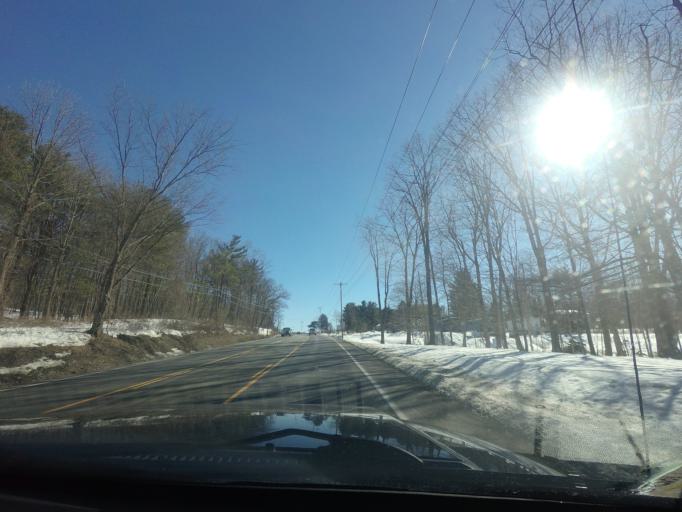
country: US
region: New York
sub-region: Rensselaer County
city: Nassau
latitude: 42.5340
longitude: -73.6594
